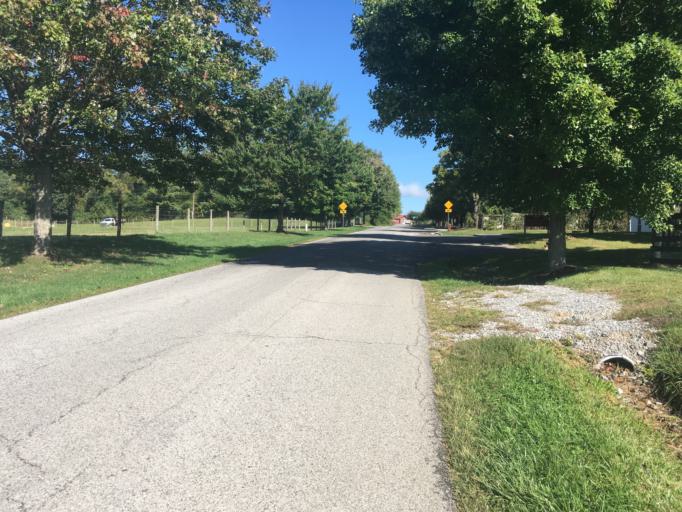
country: US
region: Virginia
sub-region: Montgomery County
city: Blacksburg
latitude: 37.2223
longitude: -80.4421
